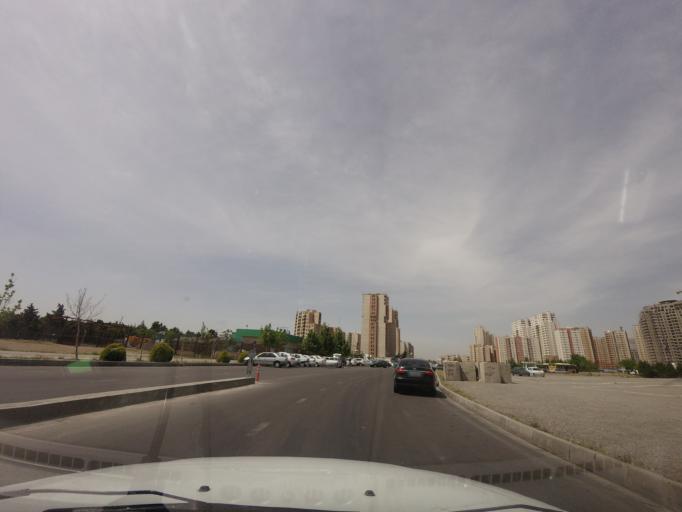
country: IR
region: Tehran
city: Shahr-e Qods
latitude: 35.7472
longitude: 51.2012
